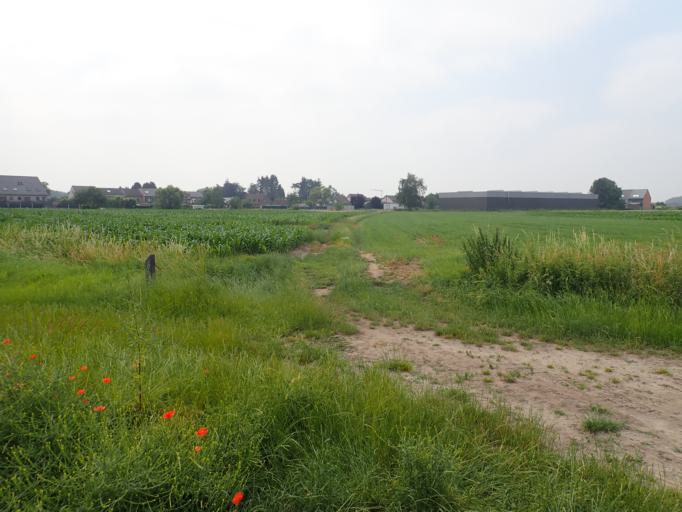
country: BE
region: Flanders
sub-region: Provincie Oost-Vlaanderen
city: Lebbeke
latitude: 51.0267
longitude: 4.1619
